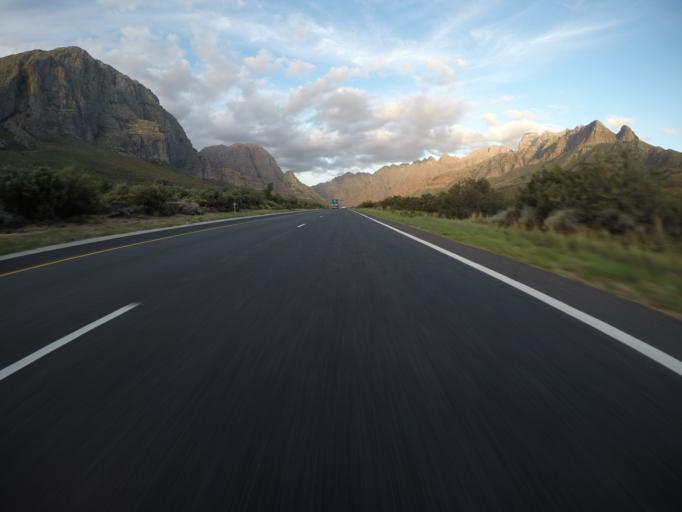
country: ZA
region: Western Cape
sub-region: Cape Winelands District Municipality
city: Paarl
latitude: -33.7265
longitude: 19.1268
